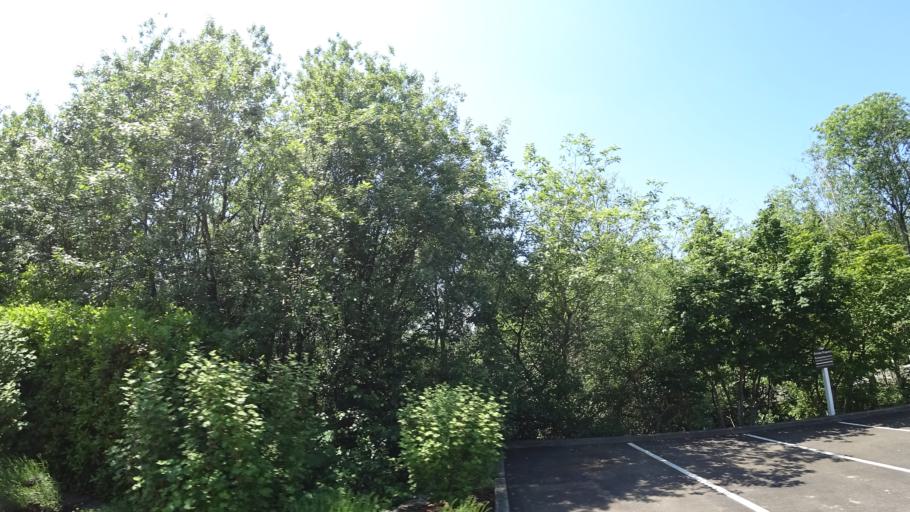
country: US
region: Oregon
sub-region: Washington County
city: Metzger
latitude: 45.4355
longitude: -122.7191
